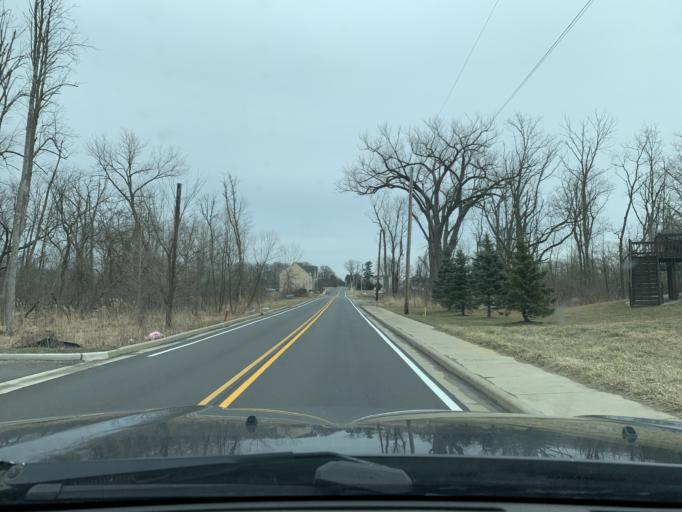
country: US
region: Indiana
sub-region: Porter County
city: Chesterton
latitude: 41.5863
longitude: -87.0388
